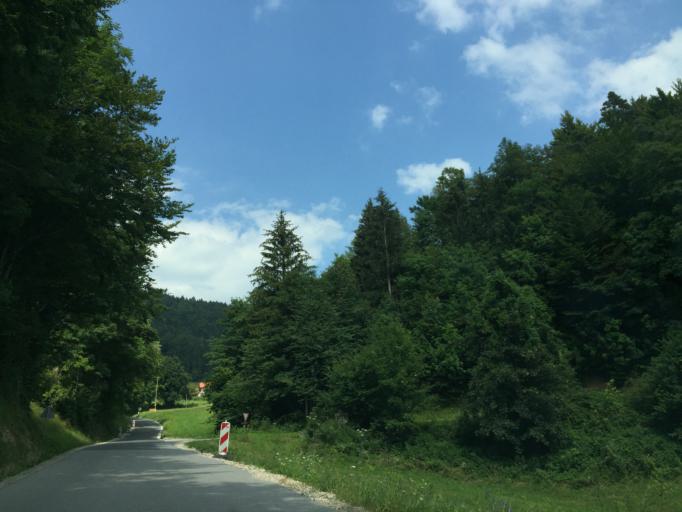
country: SI
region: Sostanj
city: Ravne
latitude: 46.4077
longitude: 15.1018
